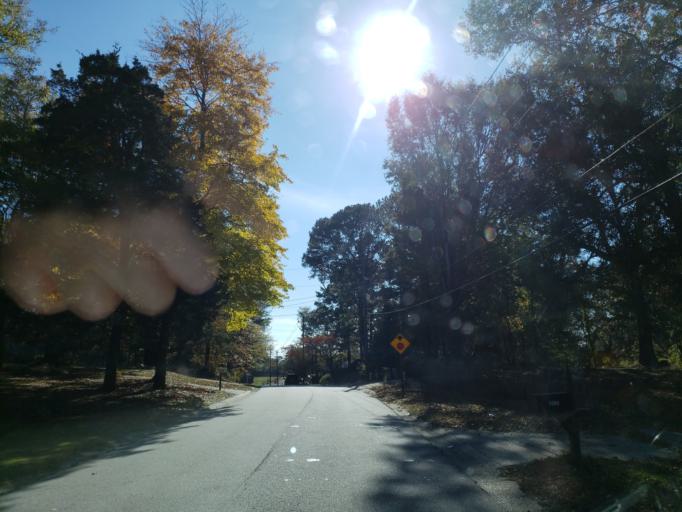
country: US
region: Georgia
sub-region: Cobb County
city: Mableton
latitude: 33.7810
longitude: -84.5466
